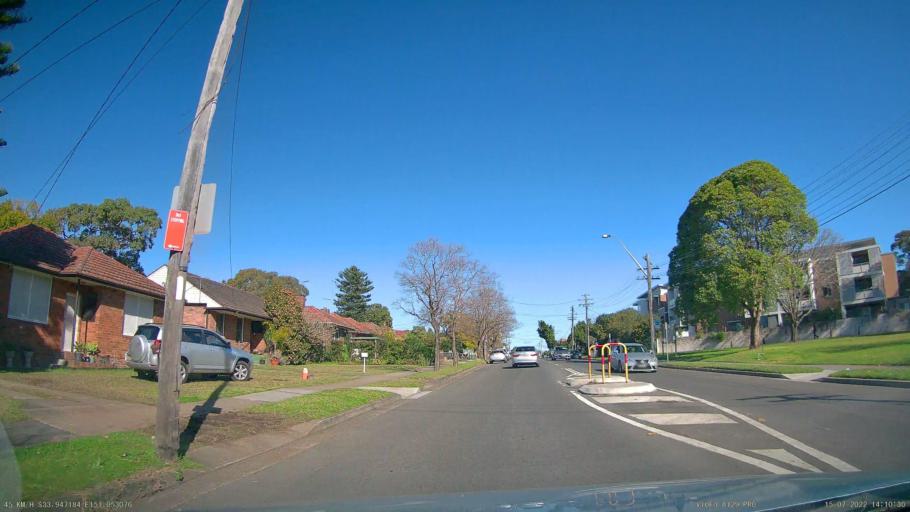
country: AU
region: New South Wales
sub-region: Hurstville
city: Peakhurst
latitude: -33.9473
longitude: 151.0531
